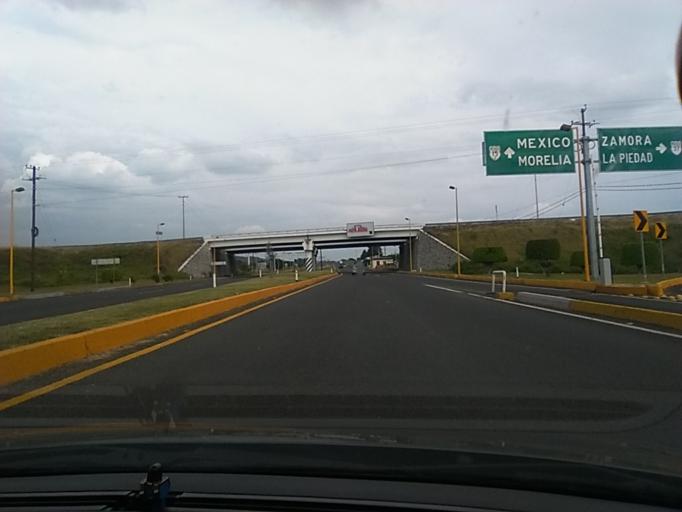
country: MX
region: Michoacan
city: Ecuandureo
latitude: 20.1750
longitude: -102.1909
